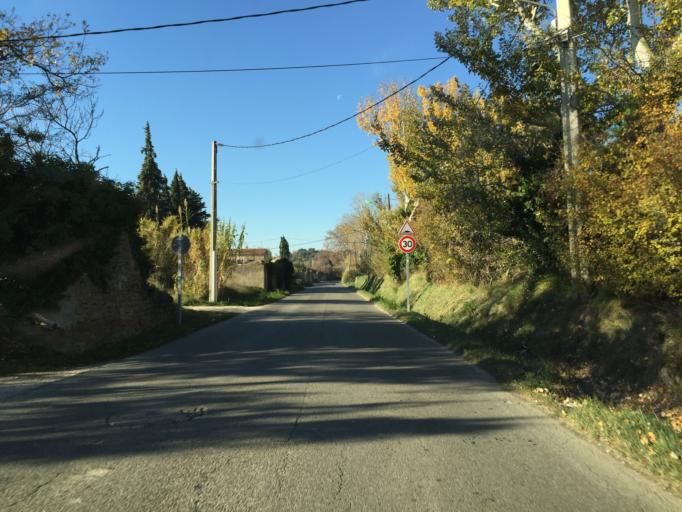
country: FR
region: Provence-Alpes-Cote d'Azur
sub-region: Departement du Vaucluse
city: Bedarrides
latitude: 44.0383
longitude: 4.9066
